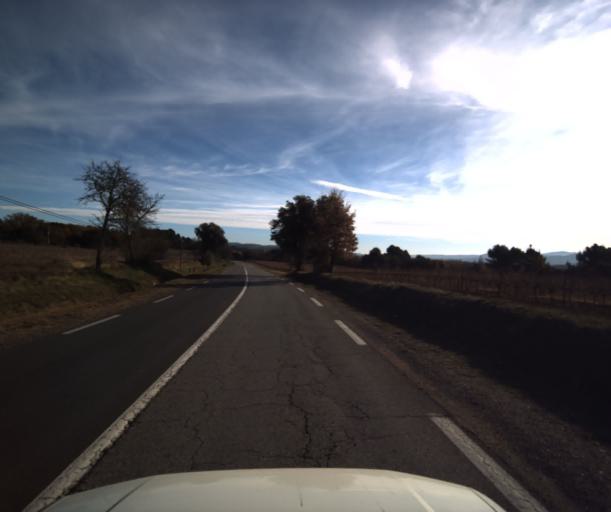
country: FR
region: Provence-Alpes-Cote d'Azur
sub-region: Departement du Vaucluse
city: Pertuis
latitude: 43.6985
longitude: 5.4657
